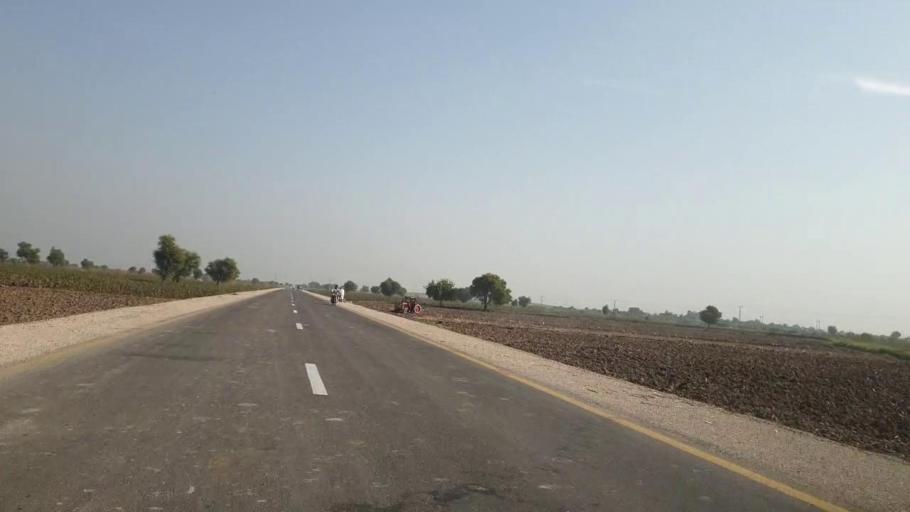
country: PK
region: Sindh
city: Sehwan
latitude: 26.4663
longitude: 67.7968
